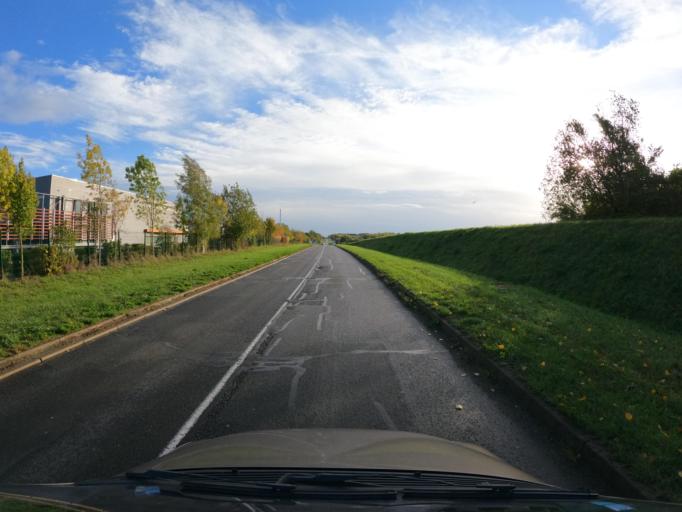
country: FR
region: Ile-de-France
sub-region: Departement de Seine-et-Marne
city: Bussy-Saint-Georges
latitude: 48.8315
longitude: 2.6956
